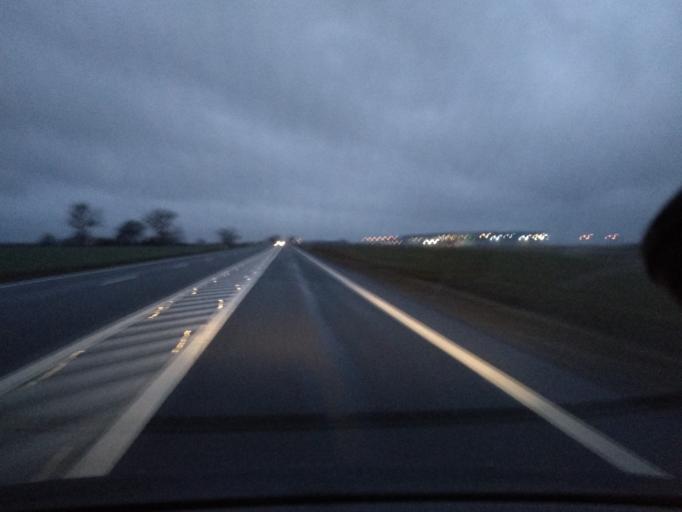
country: PL
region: Lower Silesian Voivodeship
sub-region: Powiat sredzki
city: Szczepanow
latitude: 51.1636
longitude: 16.6608
